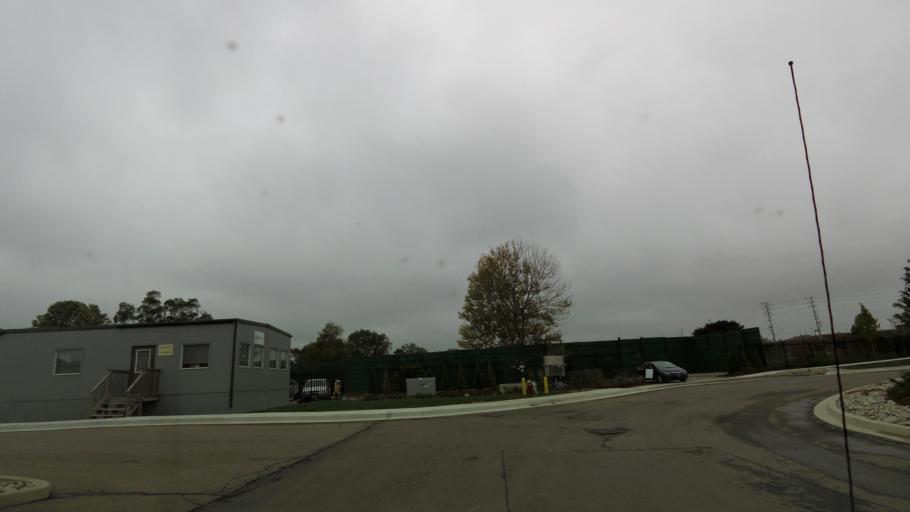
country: CA
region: Ontario
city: Etobicoke
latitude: 43.5696
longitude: -79.5610
